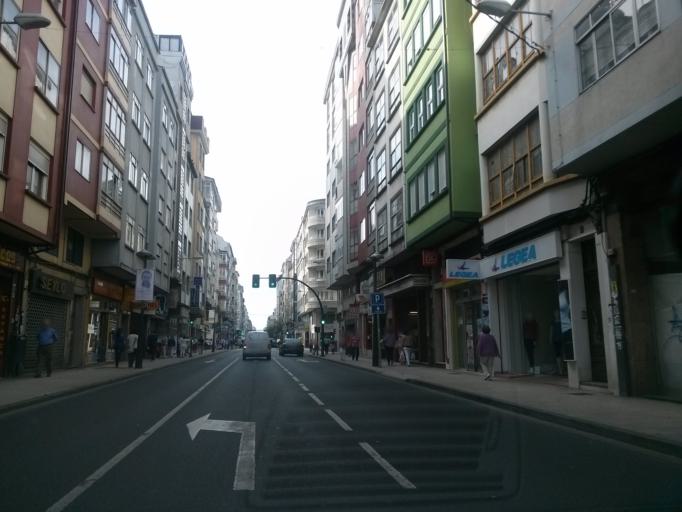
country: ES
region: Galicia
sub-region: Provincia de Lugo
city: Lugo
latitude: 43.0169
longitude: -7.5602
